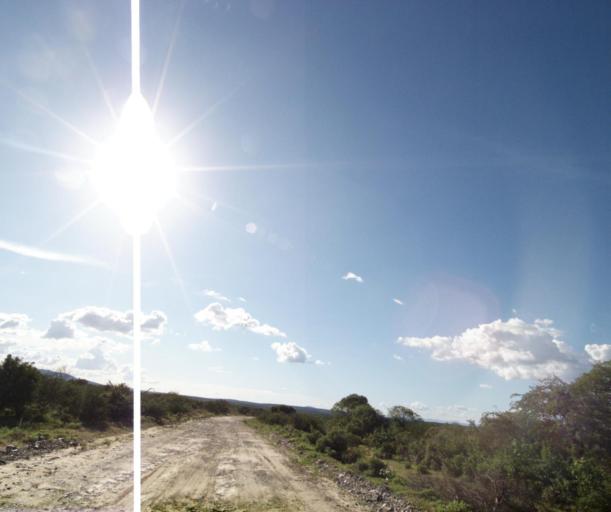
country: BR
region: Bahia
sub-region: Tanhacu
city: Tanhacu
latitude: -14.1854
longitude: -40.9953
